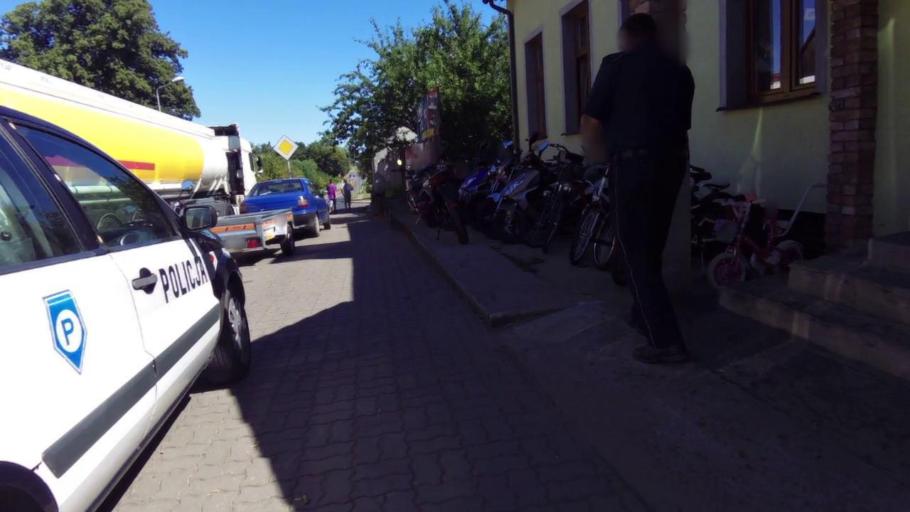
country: PL
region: West Pomeranian Voivodeship
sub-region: Powiat drawski
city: Czaplinek
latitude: 53.5593
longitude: 16.2343
